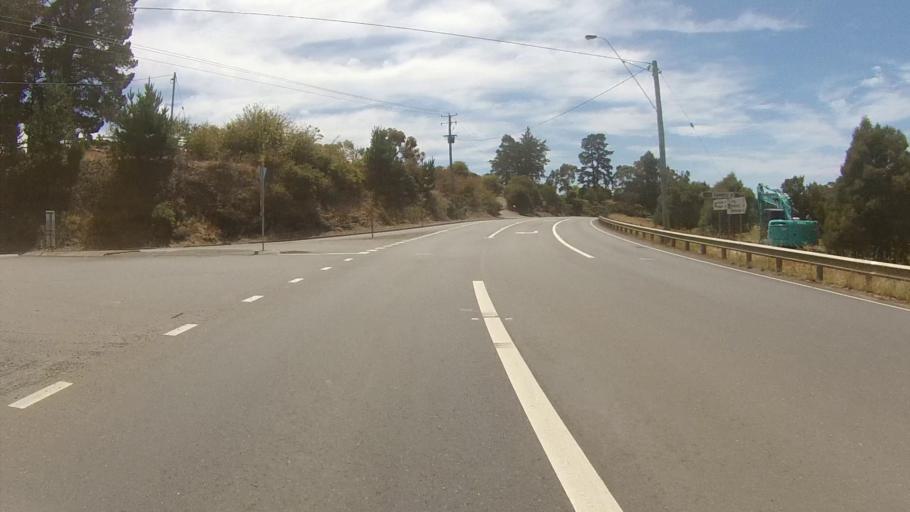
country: AU
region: Tasmania
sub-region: Kingborough
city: Margate
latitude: -43.0229
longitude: 147.2598
